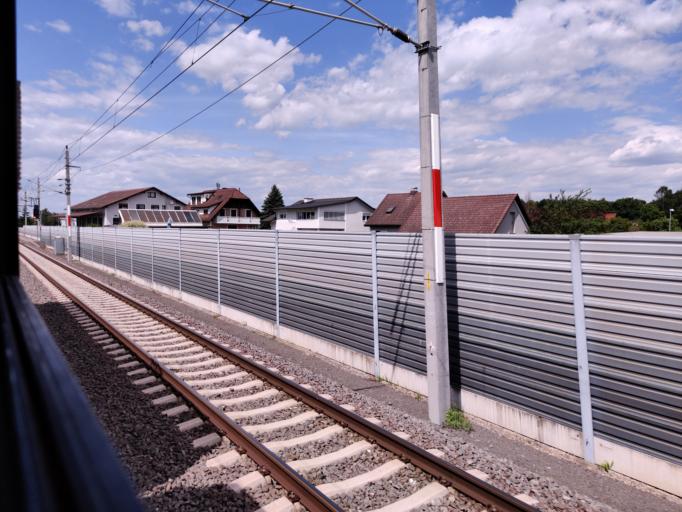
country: AT
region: Styria
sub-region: Politischer Bezirk Leibnitz
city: Kaindorf an der Sulm
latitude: 46.7913
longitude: 15.5446
